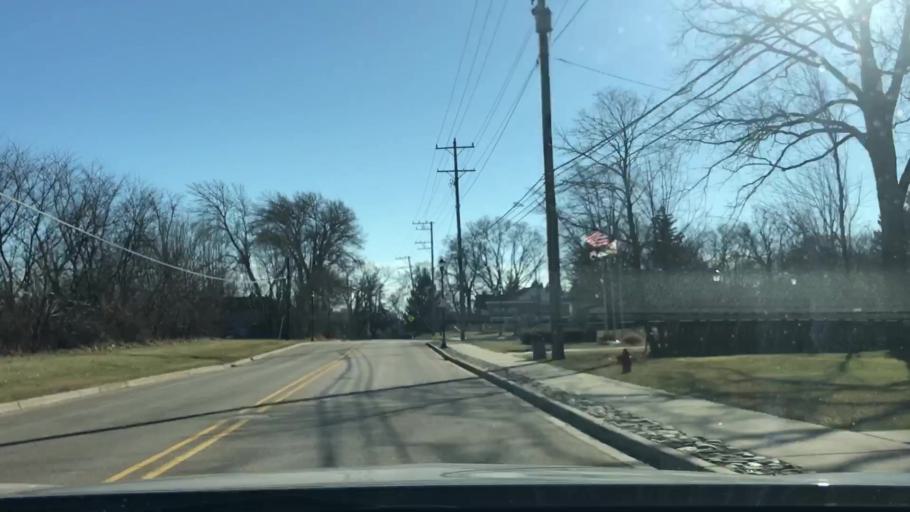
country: US
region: Illinois
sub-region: Kane County
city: Pingree Grove
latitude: 42.0717
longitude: -88.4154
